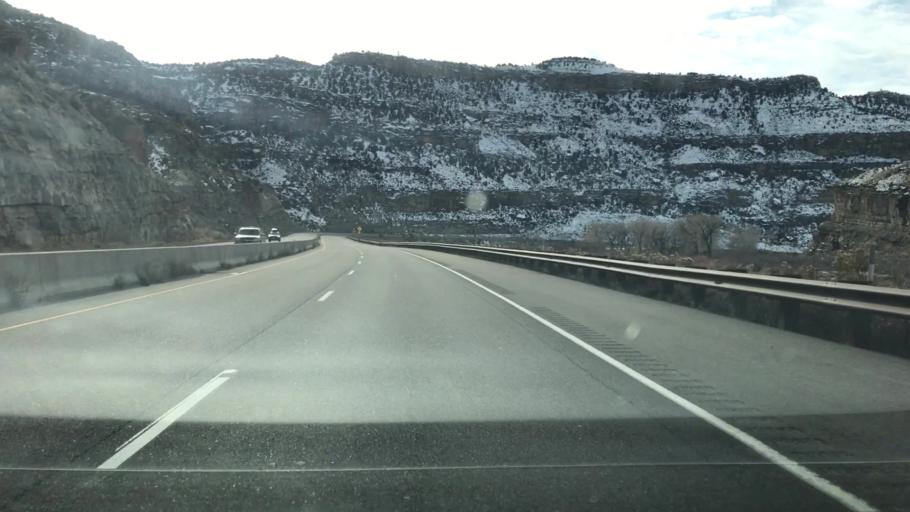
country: US
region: Colorado
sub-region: Mesa County
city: Palisade
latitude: 39.2454
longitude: -108.2562
